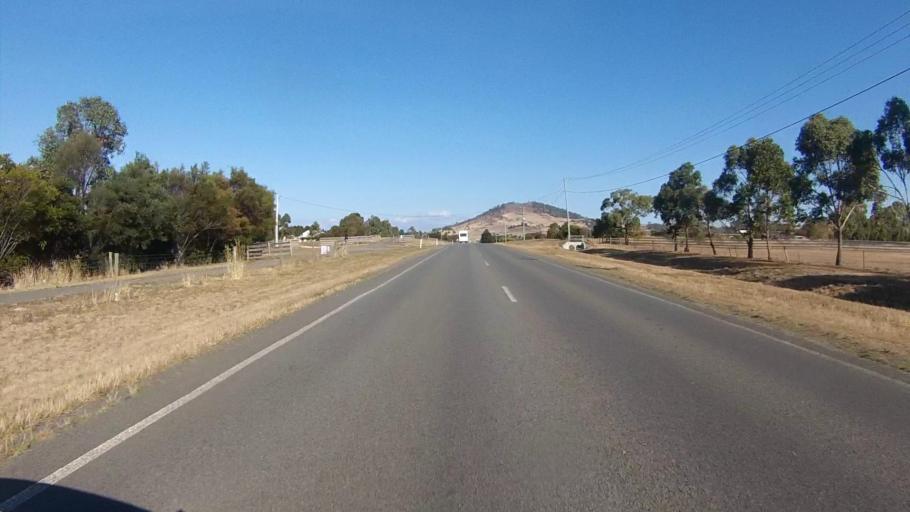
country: AU
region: Tasmania
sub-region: Clarence
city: Seven Mile Beach
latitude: -42.8507
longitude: 147.4846
